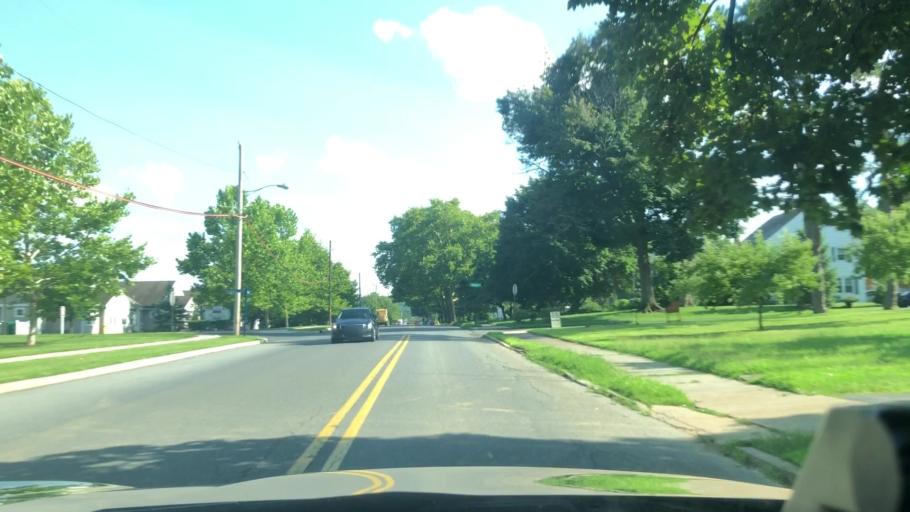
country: US
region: Pennsylvania
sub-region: Lehigh County
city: Fountain Hill
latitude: 40.6317
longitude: -75.4218
